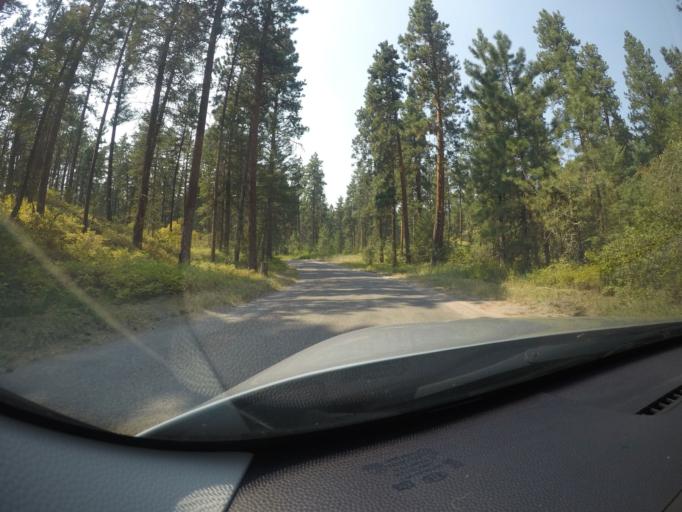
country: US
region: Montana
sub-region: Lake County
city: Polson
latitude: 47.7663
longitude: -114.1541
